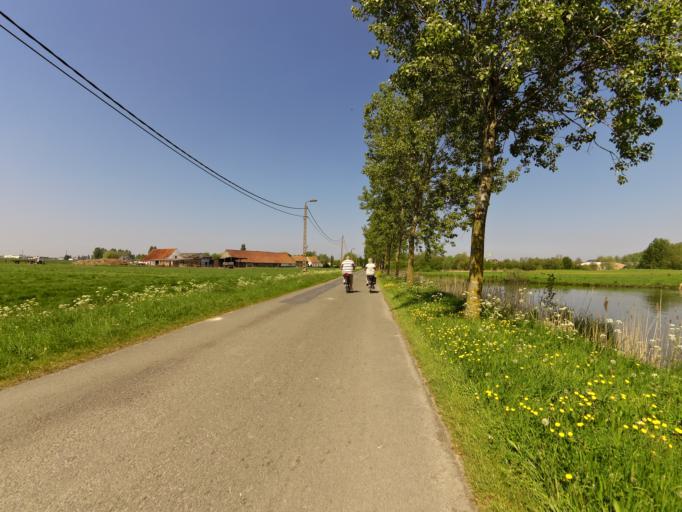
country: BE
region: Flanders
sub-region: Provincie West-Vlaanderen
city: Ostend
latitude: 51.1992
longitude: 2.9181
